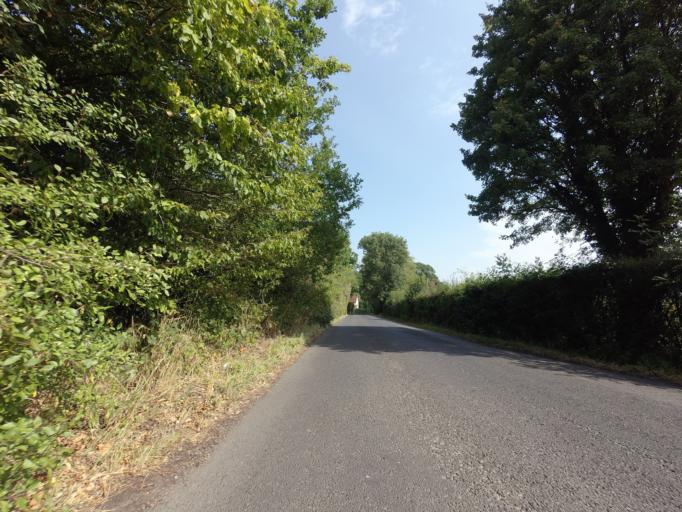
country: GB
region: England
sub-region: Kent
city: Staplehurst
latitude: 51.1299
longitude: 0.5791
